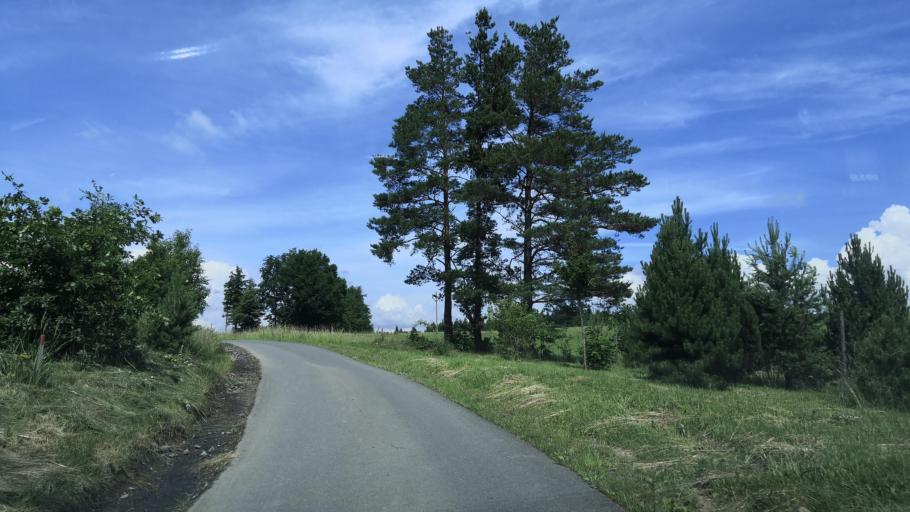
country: CZ
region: Zlin
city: Vidce
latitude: 49.4268
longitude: 18.0962
